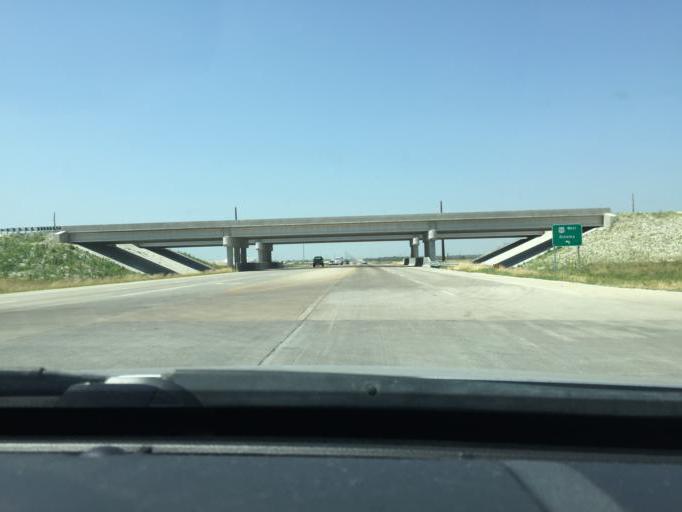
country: US
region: Kansas
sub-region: Reno County
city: Hutchinson
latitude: 38.0276
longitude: -97.8668
